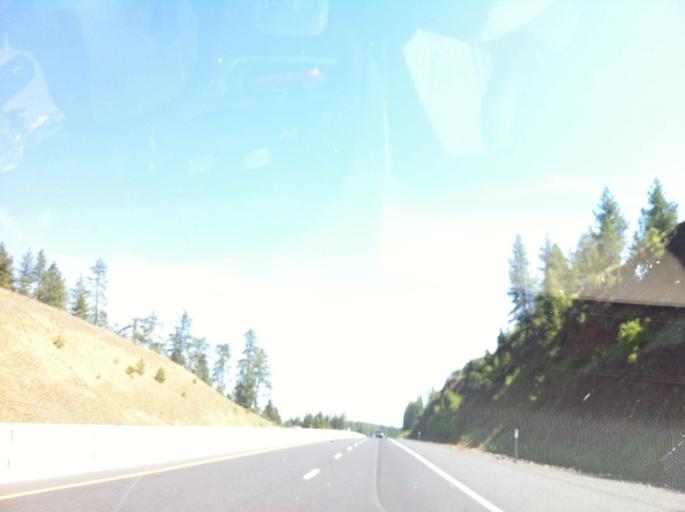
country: US
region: Oregon
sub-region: Umatilla County
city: Mission
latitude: 45.4802
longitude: -118.4020
